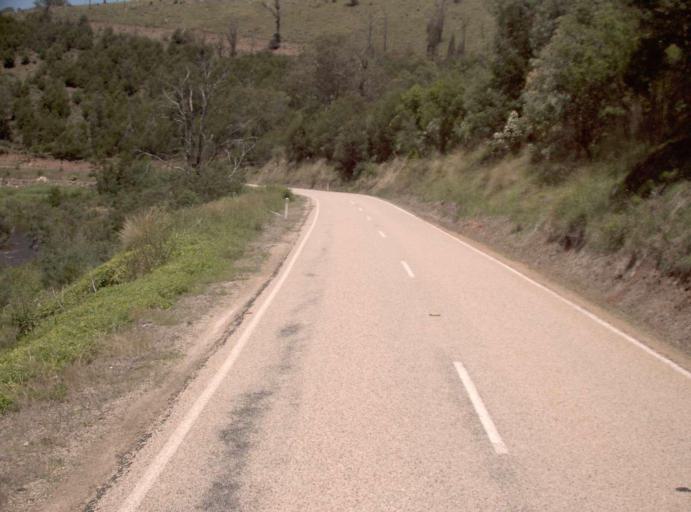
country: AU
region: Victoria
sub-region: East Gippsland
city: Bairnsdale
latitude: -37.5268
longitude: 147.8433
